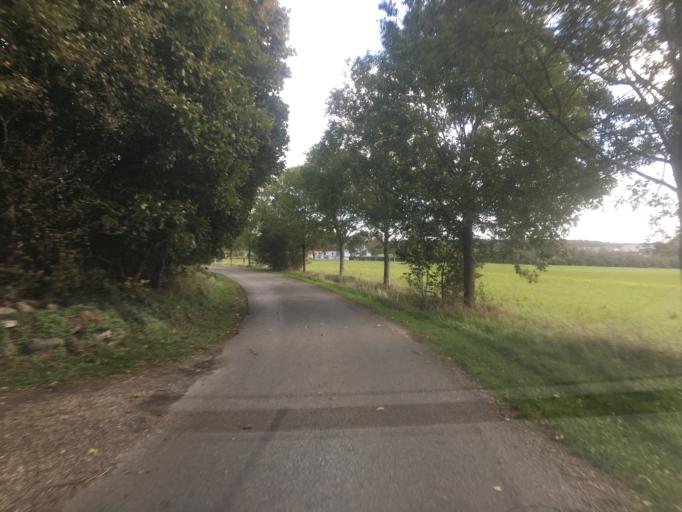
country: DK
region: South Denmark
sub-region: Tonder Kommune
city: Logumkloster
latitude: 55.1139
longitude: 8.8806
